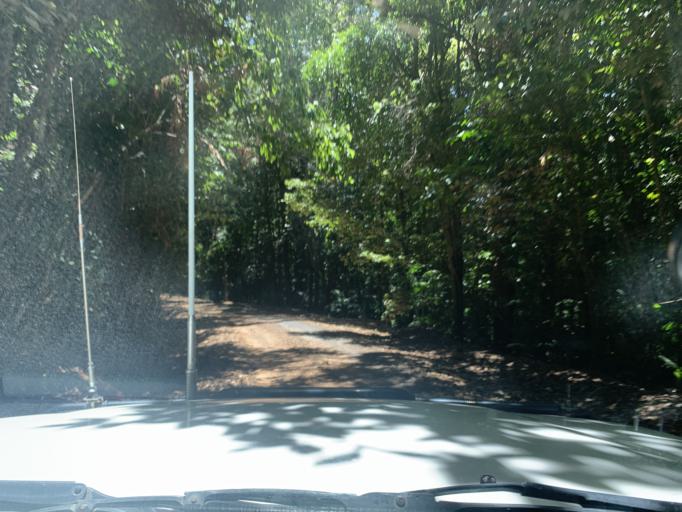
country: AU
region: Queensland
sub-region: Cairns
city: Redlynch
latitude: -16.9571
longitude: 145.6418
